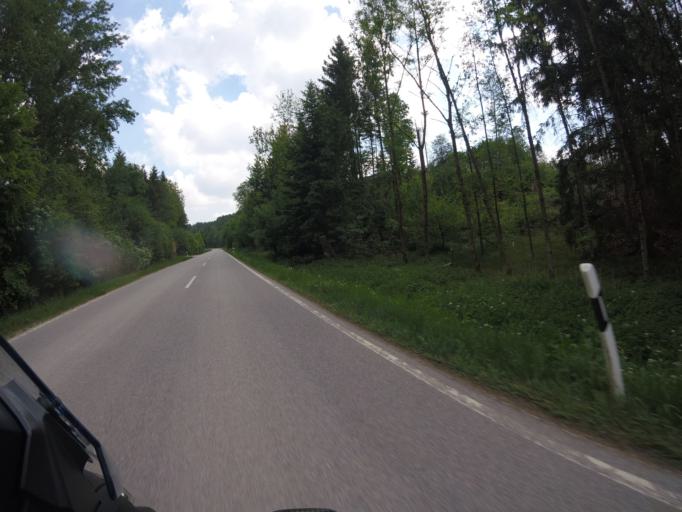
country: DE
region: Bavaria
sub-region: Lower Bavaria
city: Attenhofen
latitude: 48.6426
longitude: 11.8676
